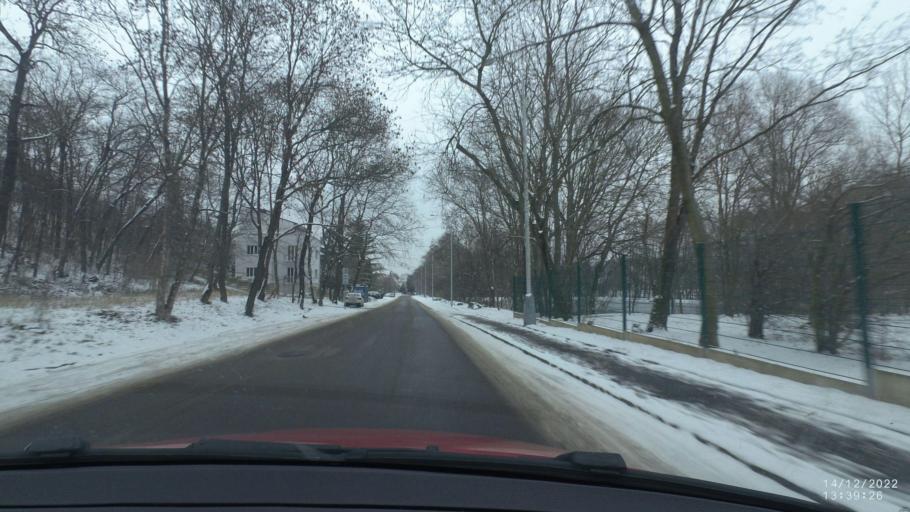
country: CZ
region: Central Bohemia
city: Horomerice
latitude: 50.0696
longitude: 14.3393
